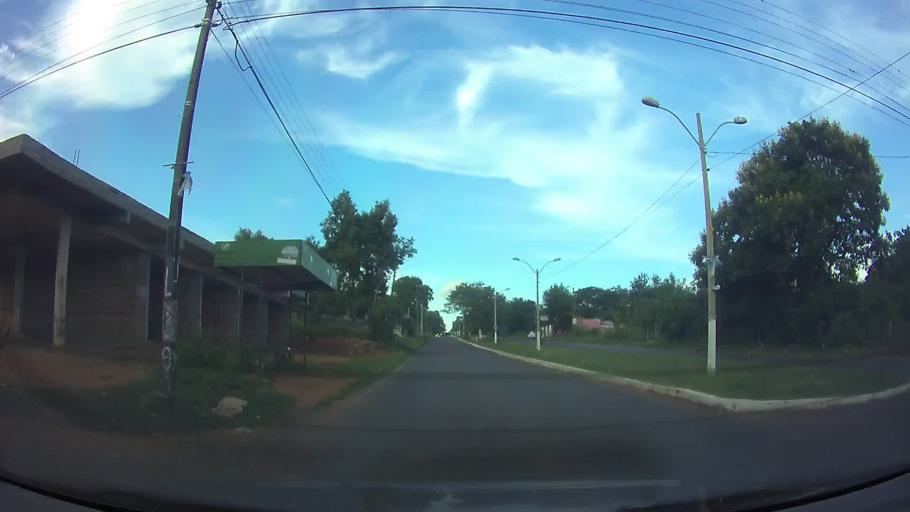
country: PY
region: Central
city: San Antonio
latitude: -25.4304
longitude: -57.5489
